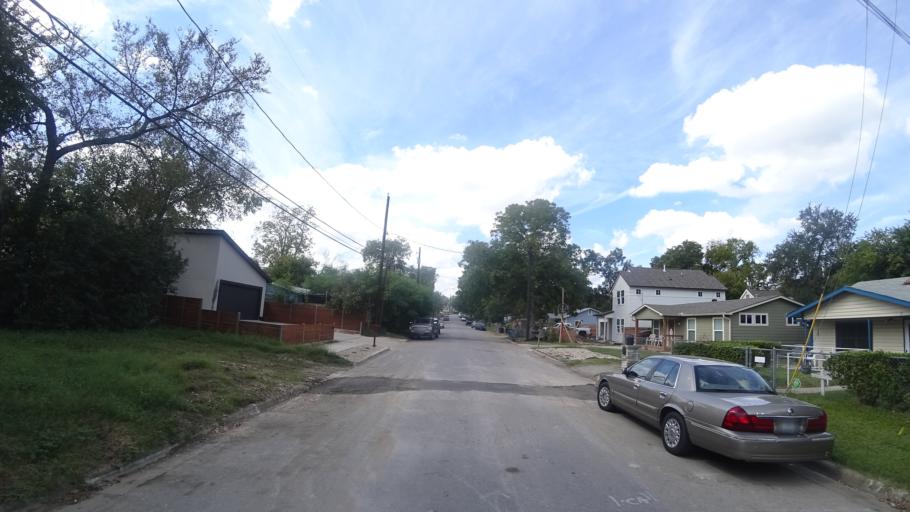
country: US
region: Texas
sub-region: Travis County
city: Austin
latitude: 30.2630
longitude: -97.7100
